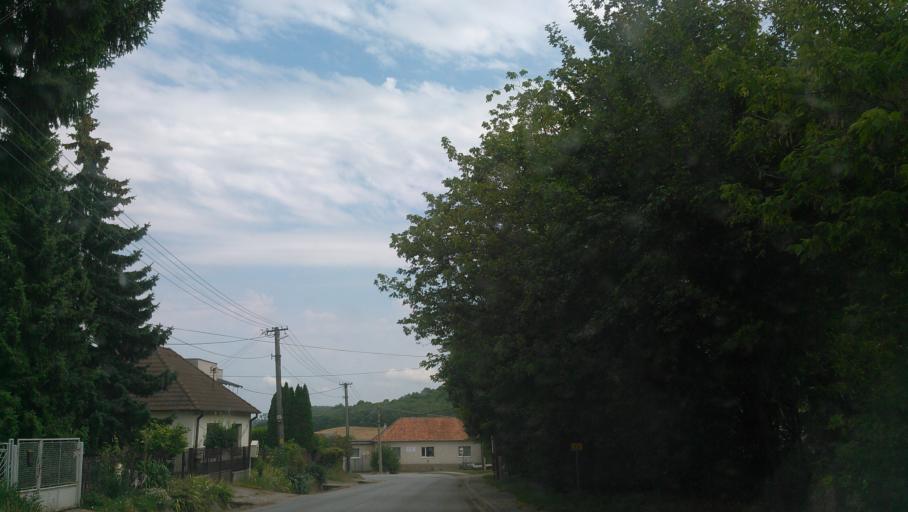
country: SK
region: Trnavsky
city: Hlohovec
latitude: 48.4407
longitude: 17.8878
